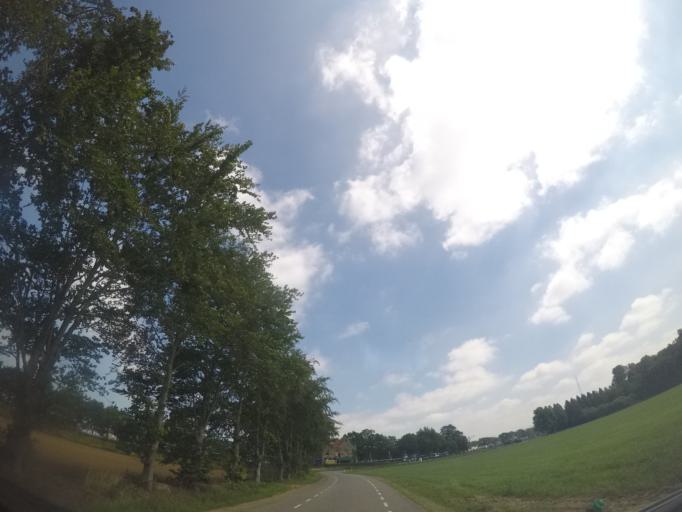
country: NL
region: Overijssel
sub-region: Gemeente Dalfsen
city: Dalfsen
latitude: 52.4976
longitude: 6.2581
